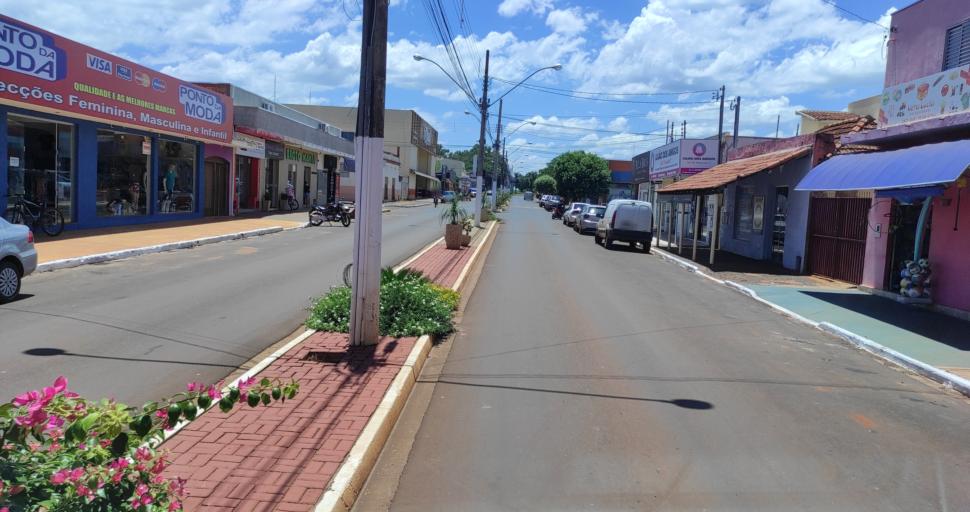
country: BR
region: Minas Gerais
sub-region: Frutal
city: Frutal
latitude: -20.1388
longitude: -48.7009
